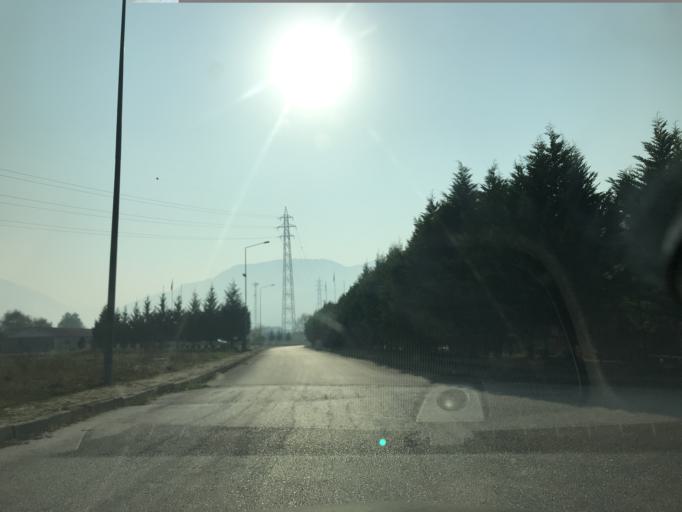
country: TR
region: Duzce
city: Duzce
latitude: 40.7856
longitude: 31.1532
